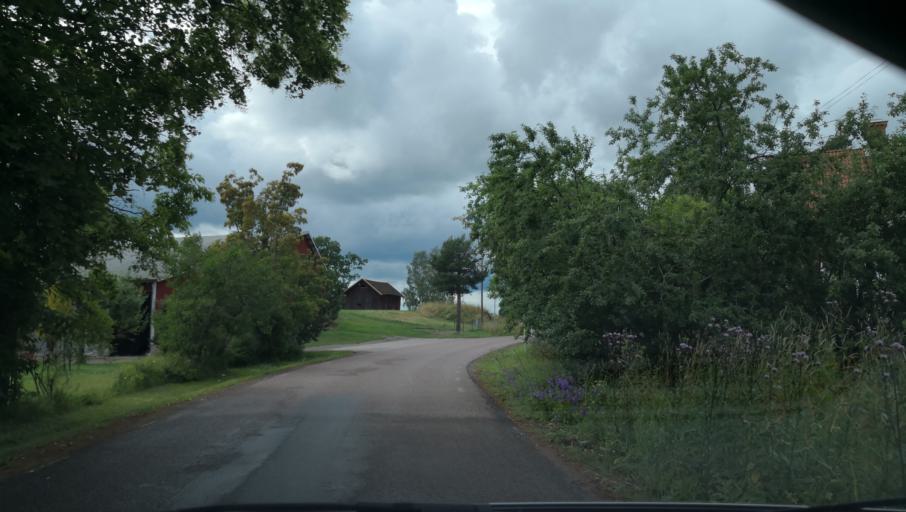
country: SE
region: Dalarna
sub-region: Borlange Kommun
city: Ornas
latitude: 60.4442
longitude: 15.5869
